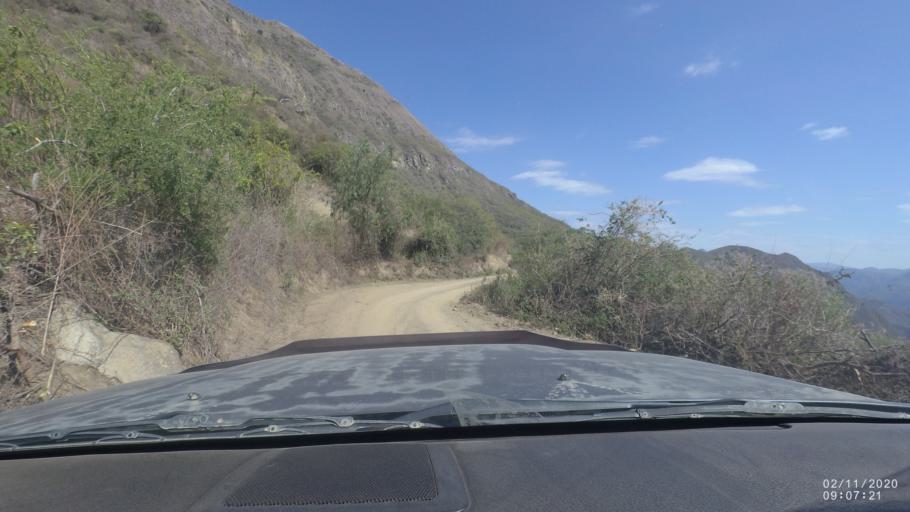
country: BO
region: Chuquisaca
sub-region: Provincia Zudanez
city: Mojocoya
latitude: -18.5305
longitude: -64.5606
